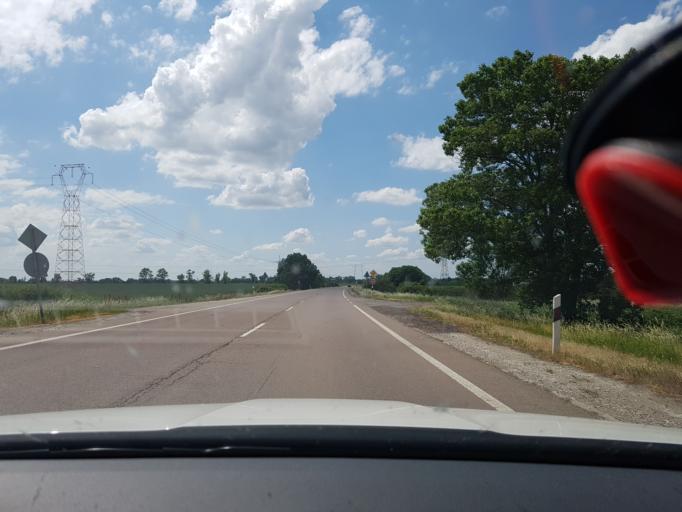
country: HU
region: Heves
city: Domoszlo
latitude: 47.7405
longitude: 20.1276
